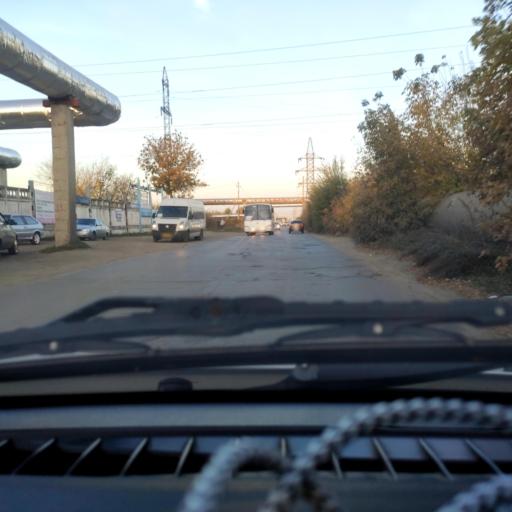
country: RU
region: Samara
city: Tol'yatti
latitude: 53.5447
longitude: 49.4439
